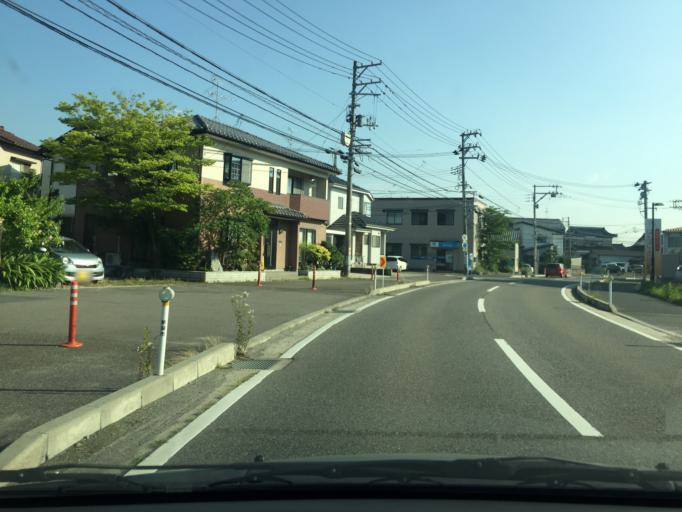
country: JP
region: Niigata
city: Niigata-shi
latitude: 37.8867
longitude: 139.0409
